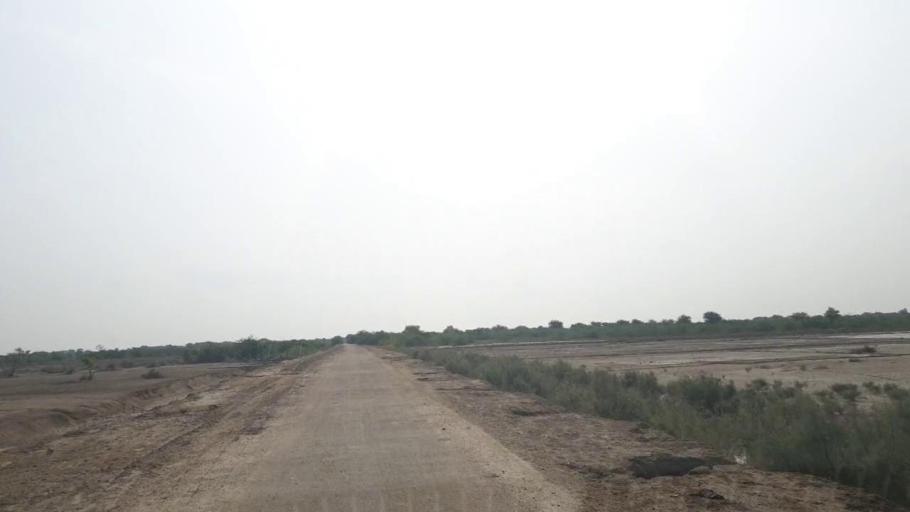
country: PK
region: Sindh
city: Badin
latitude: 24.5529
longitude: 68.6878
